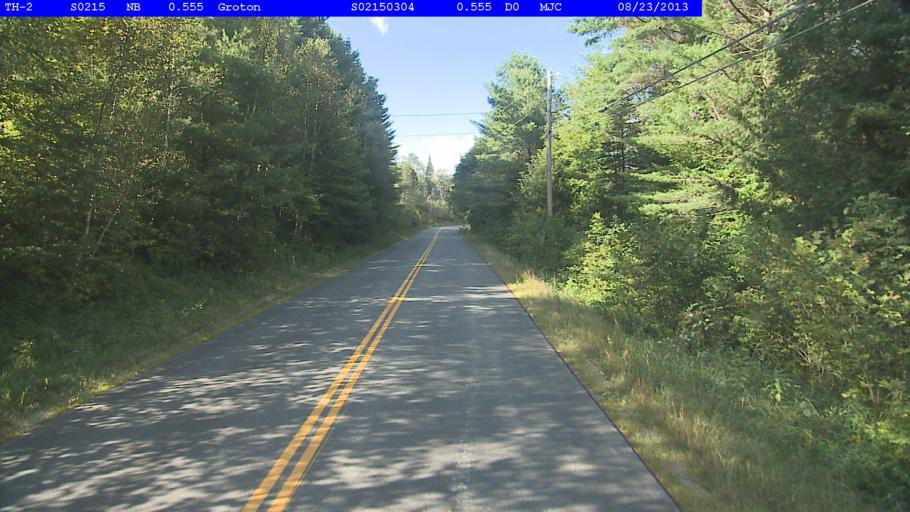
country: US
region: New Hampshire
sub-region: Grafton County
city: Woodsville
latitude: 44.2169
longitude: -72.1918
